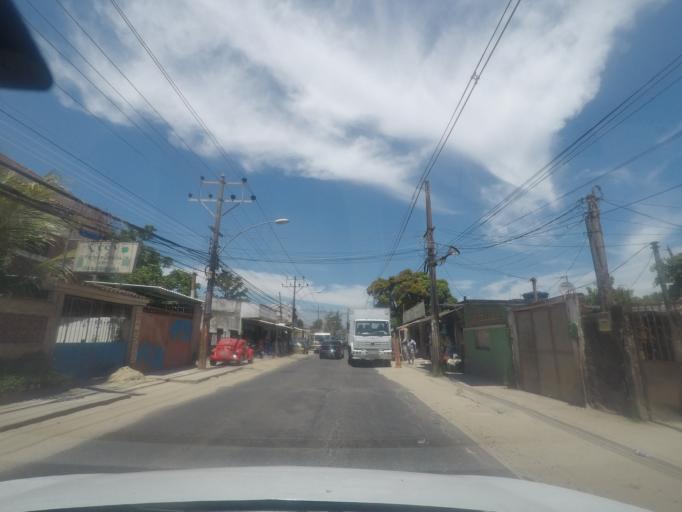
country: BR
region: Rio de Janeiro
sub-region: Itaguai
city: Itaguai
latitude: -22.9779
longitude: -43.6764
